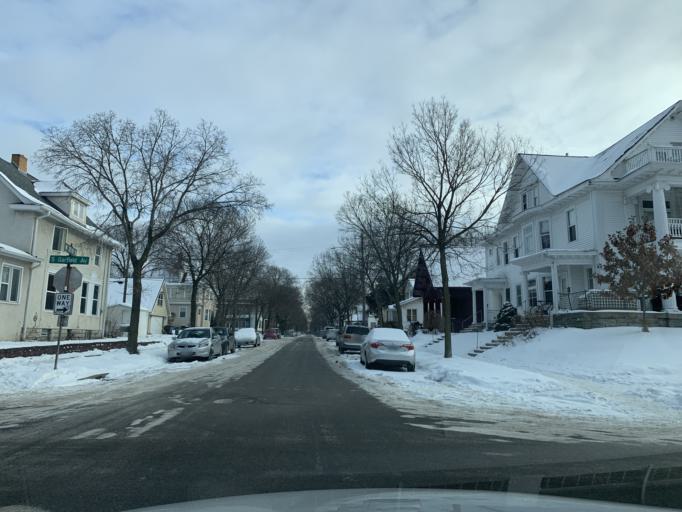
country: US
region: Minnesota
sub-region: Hennepin County
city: Minneapolis
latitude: 44.9573
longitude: -93.2869
